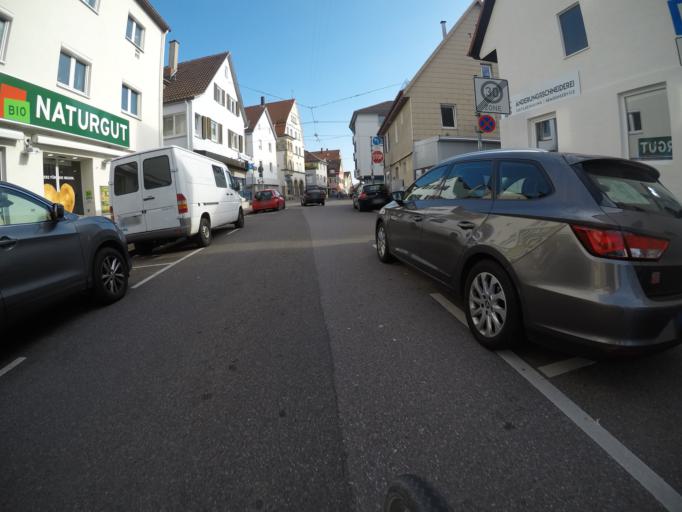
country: DE
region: Baden-Wuerttemberg
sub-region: Regierungsbezirk Stuttgart
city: Stuttgart
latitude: 48.7474
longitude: 9.1698
